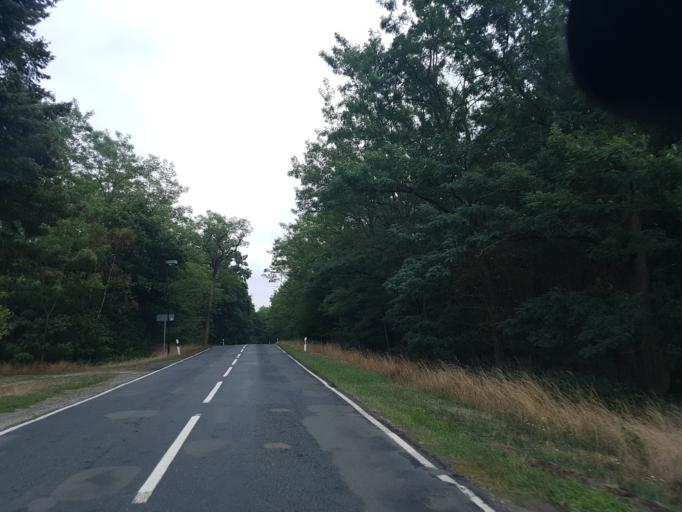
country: DE
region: Saxony-Anhalt
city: Tucheim
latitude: 52.2238
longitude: 12.1027
